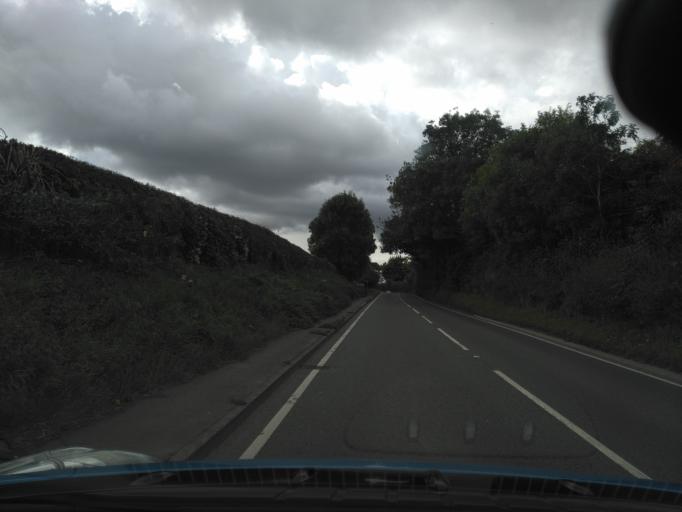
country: GB
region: England
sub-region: Oxfordshire
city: Harwell
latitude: 51.6000
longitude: -1.3480
